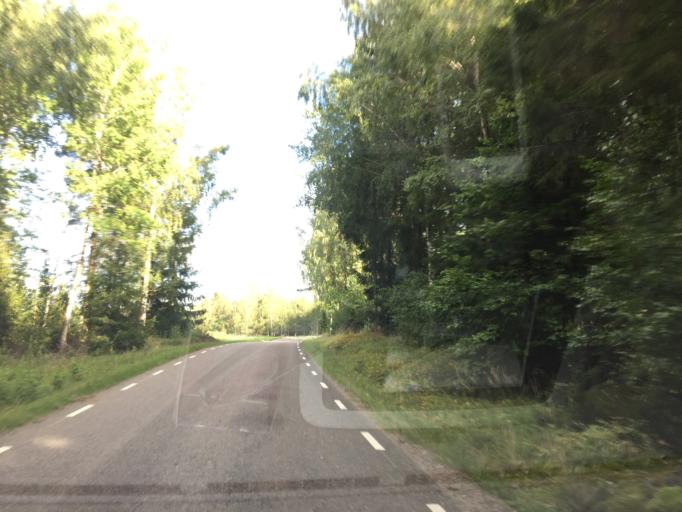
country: SE
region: Soedermanland
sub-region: Vingakers Kommun
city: Vingaker
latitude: 59.0071
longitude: 15.7549
